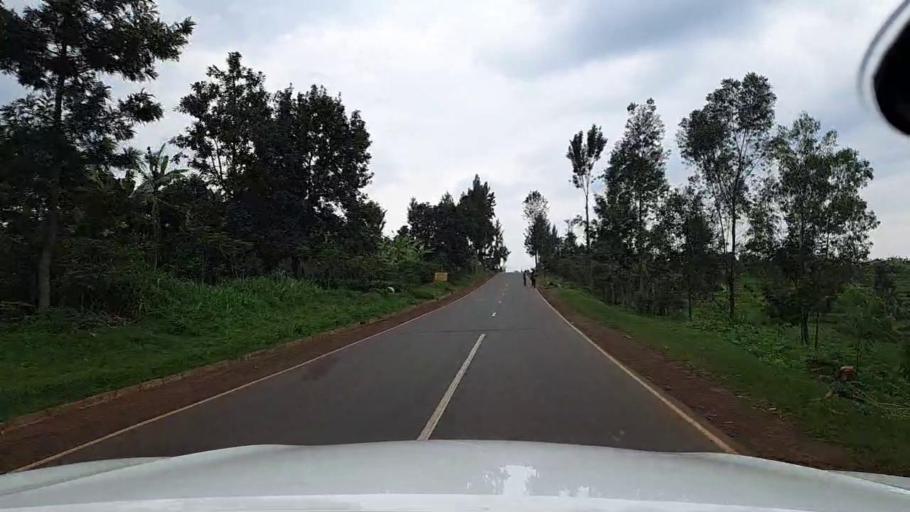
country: RW
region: Western Province
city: Cyangugu
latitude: -2.5939
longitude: 28.9307
